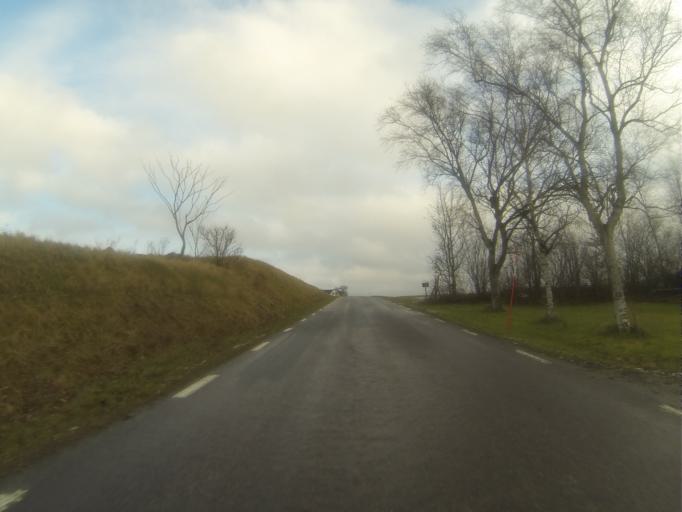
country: SE
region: Skane
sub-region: Svedala Kommun
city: Klagerup
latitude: 55.5933
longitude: 13.3014
